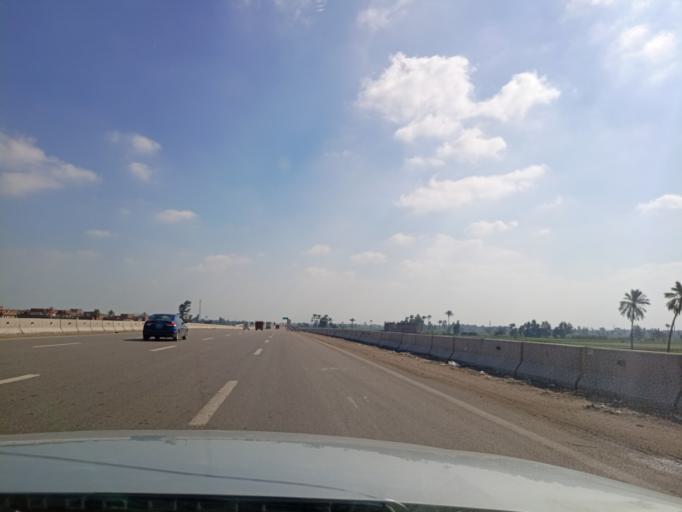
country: EG
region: Eastern Province
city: Mashtul as Suq
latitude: 30.4599
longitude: 31.3860
